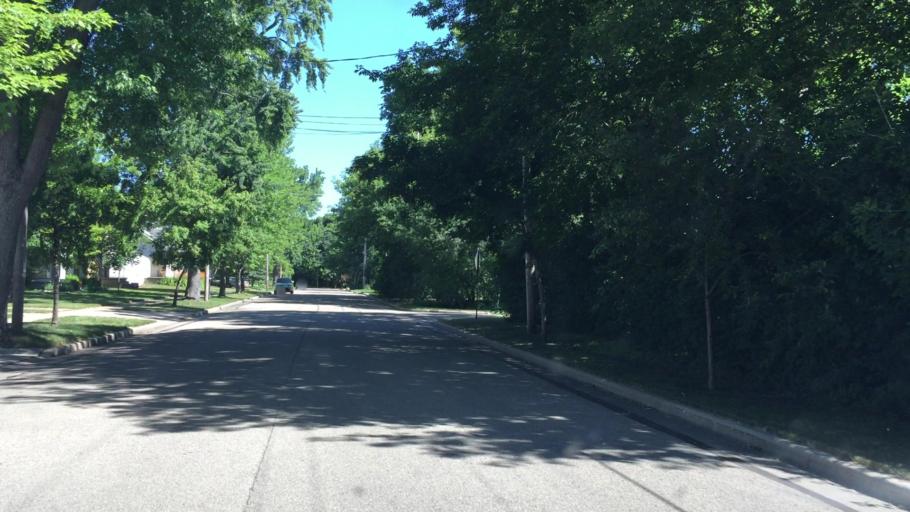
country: US
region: Wisconsin
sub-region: Winnebago County
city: Menasha
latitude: 44.1883
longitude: -88.4472
